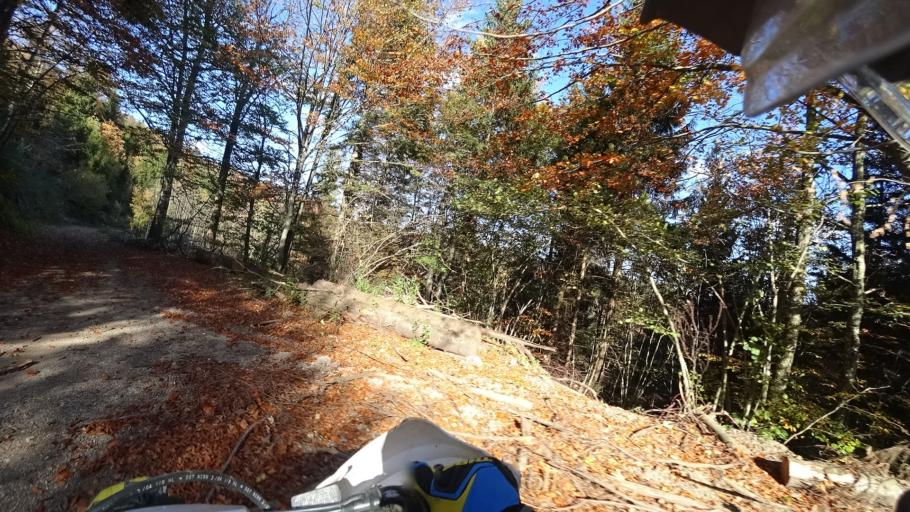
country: HR
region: Karlovacka
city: Plaski
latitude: 45.0405
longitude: 15.3483
